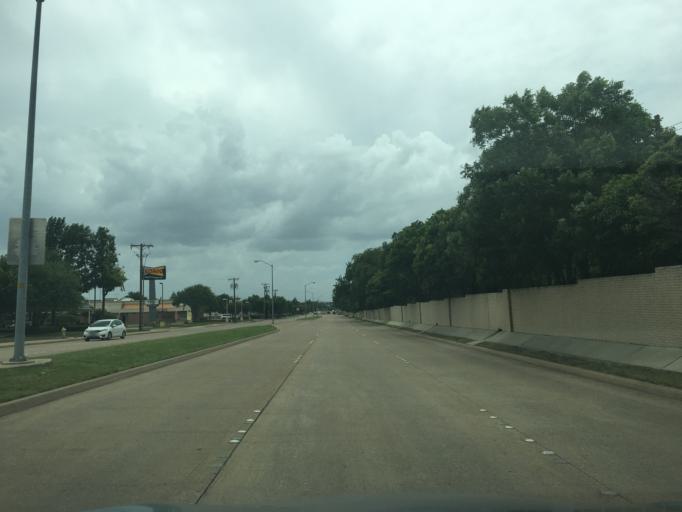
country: US
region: Texas
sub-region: Dallas County
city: Richardson
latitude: 32.9383
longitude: -96.7216
